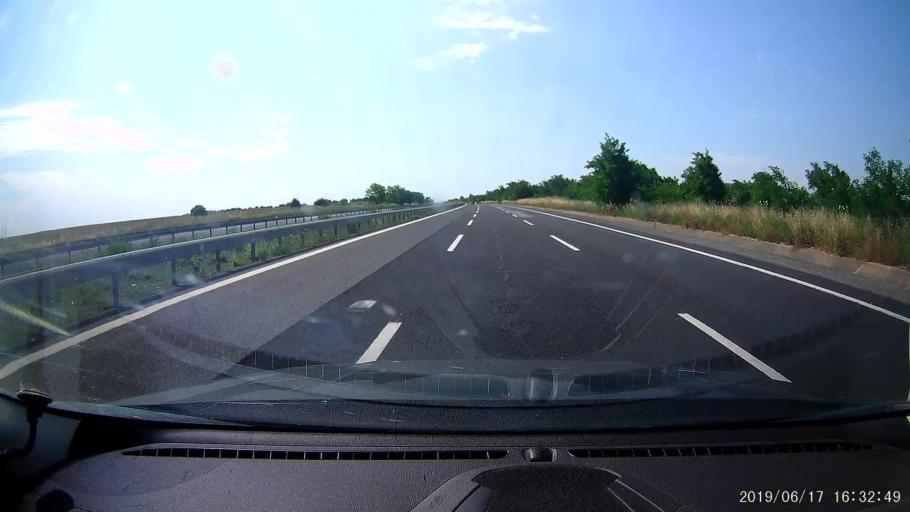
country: TR
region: Kirklareli
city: Buyukkaristiran
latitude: 41.3743
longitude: 27.5908
